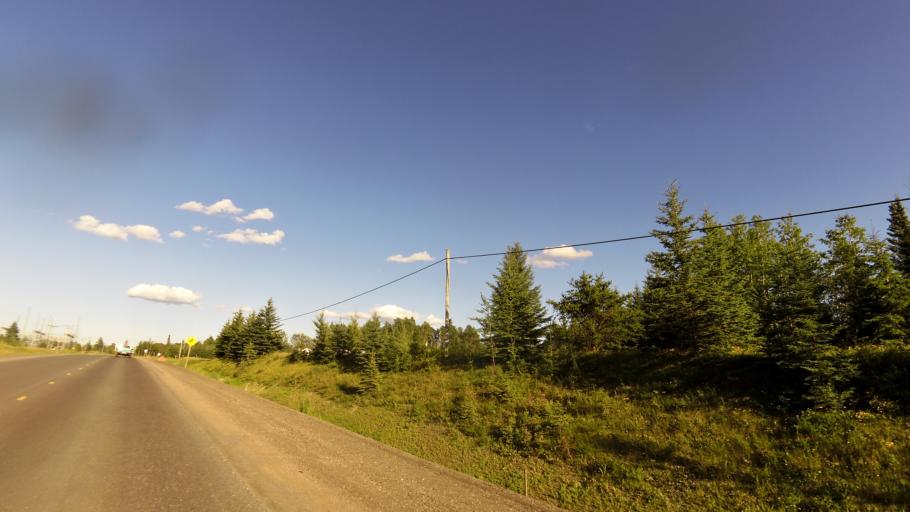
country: CA
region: Ontario
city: Dryden
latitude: 49.8151
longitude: -92.8558
